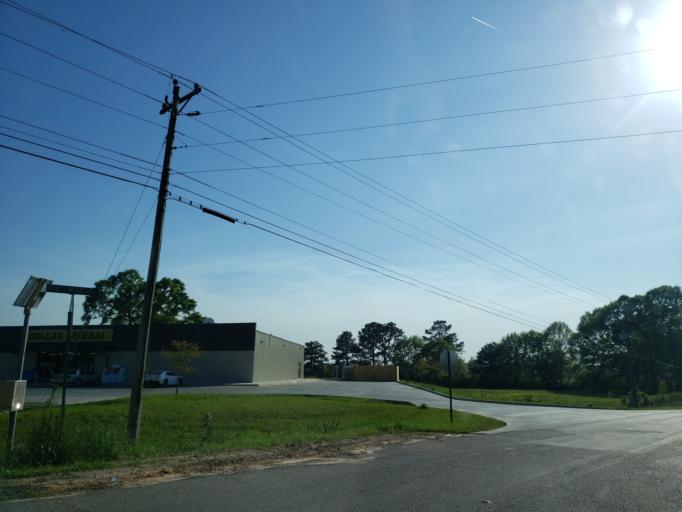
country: US
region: Mississippi
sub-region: Perry County
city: Richton
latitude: 31.4826
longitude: -89.0166
